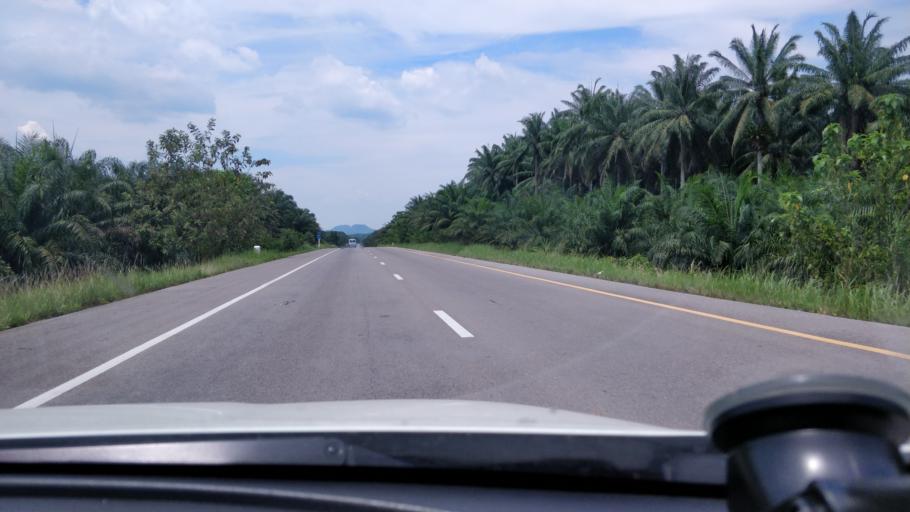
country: TH
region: Krabi
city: Plai Phraya
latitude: 8.5276
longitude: 98.8984
